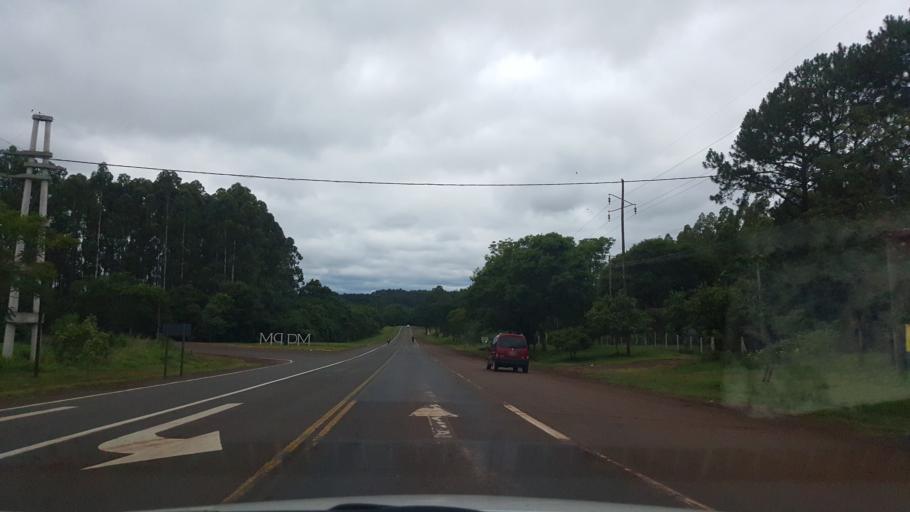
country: AR
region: Misiones
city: Capiovi
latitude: -26.9412
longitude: -55.0804
